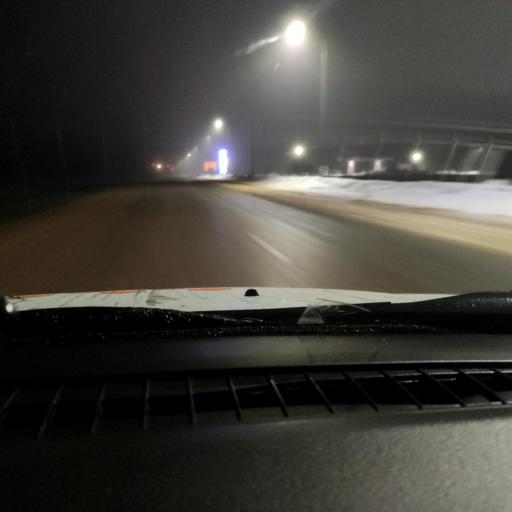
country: RU
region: Samara
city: Dubovyy Umet
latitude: 53.0096
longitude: 50.2427
